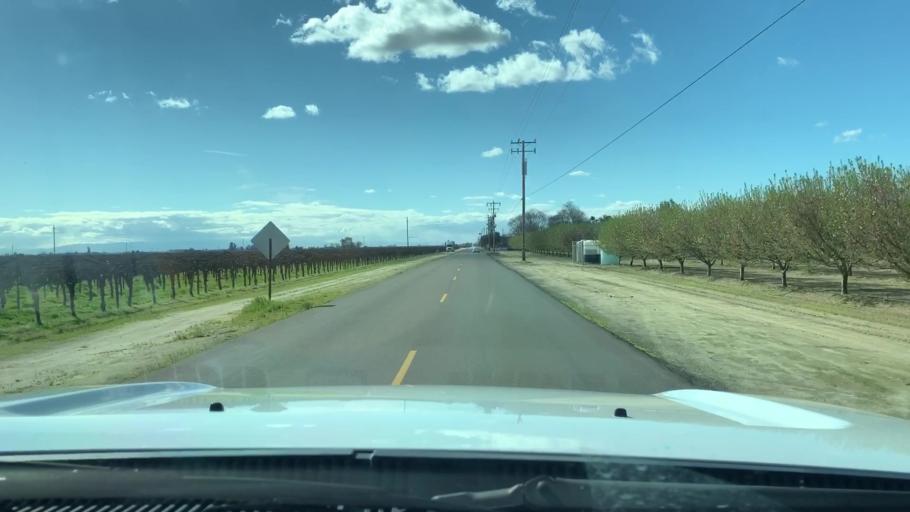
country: US
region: California
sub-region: Fresno County
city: Caruthers
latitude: 36.5619
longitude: -119.7566
